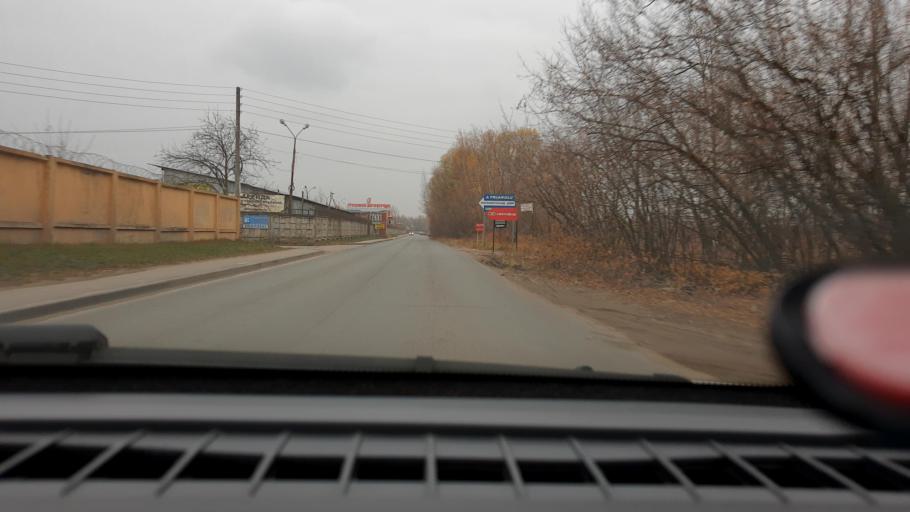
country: RU
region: Nizjnij Novgorod
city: Gorbatovka
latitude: 56.3369
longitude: 43.8063
